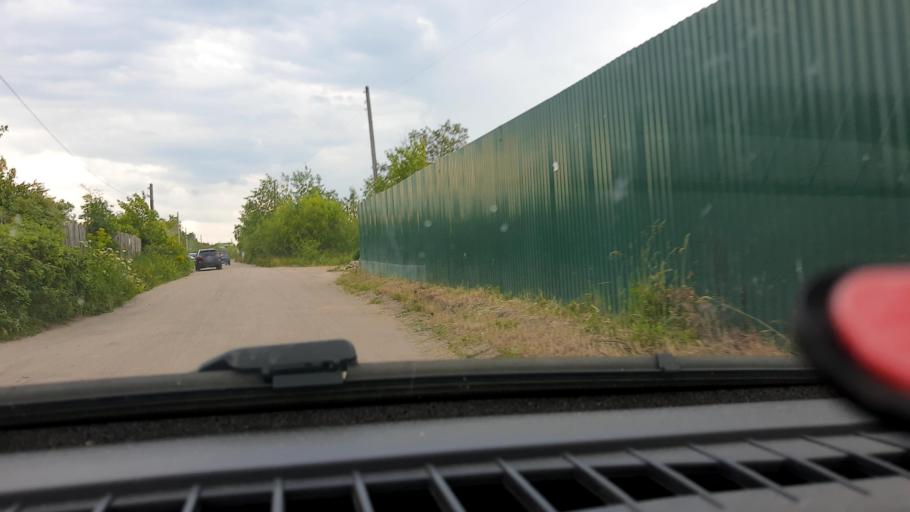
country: RU
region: Nizjnij Novgorod
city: Gorodets
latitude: 56.6597
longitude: 43.4332
